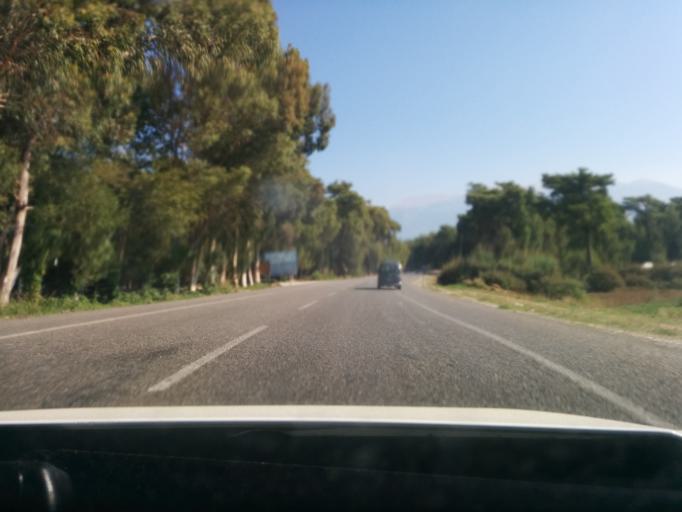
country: TR
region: Mugla
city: Esen
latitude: 36.4700
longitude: 29.2935
